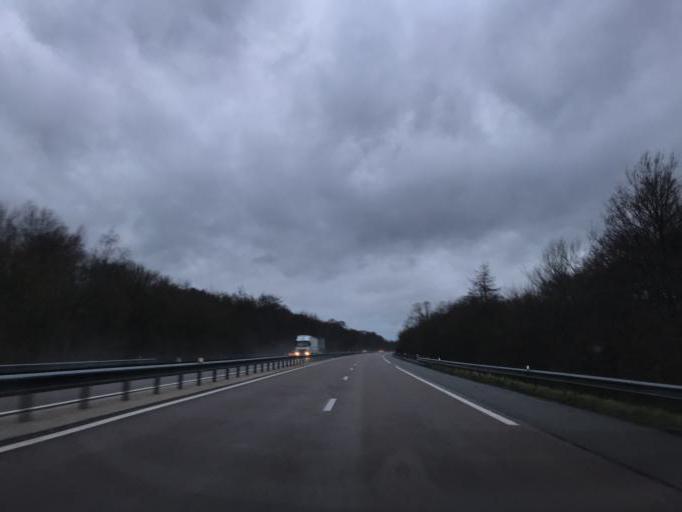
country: FR
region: Franche-Comte
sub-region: Departement du Jura
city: Damparis
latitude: 47.0992
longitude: 5.4020
